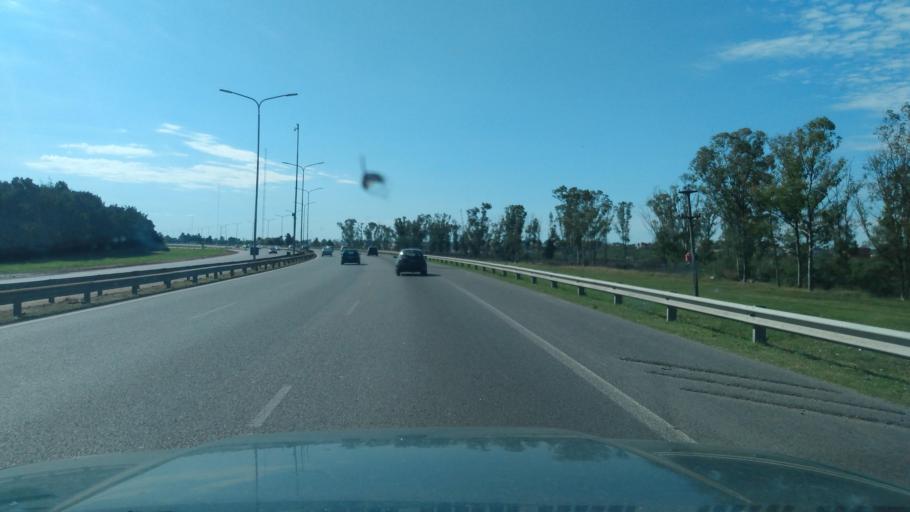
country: AR
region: Buenos Aires
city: Hurlingham
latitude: -34.5496
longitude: -58.6068
